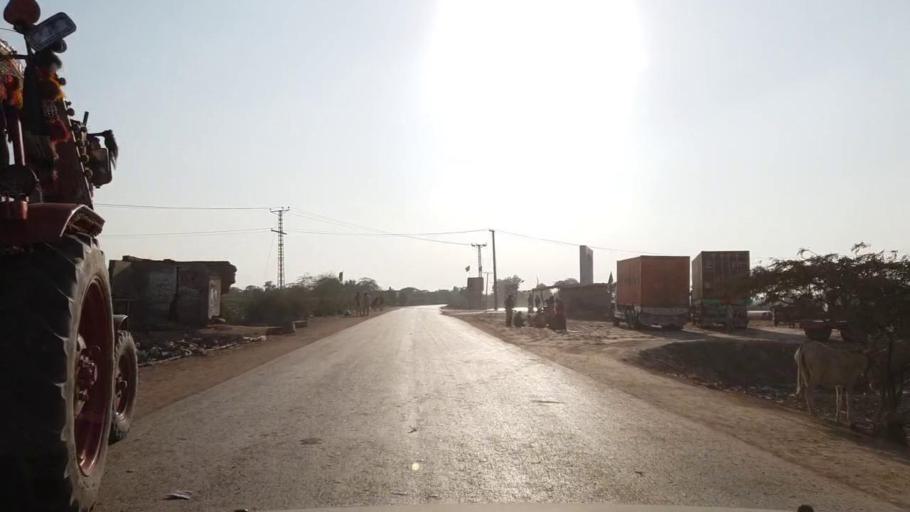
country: PK
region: Sindh
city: Bulri
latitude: 24.8097
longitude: 68.3180
